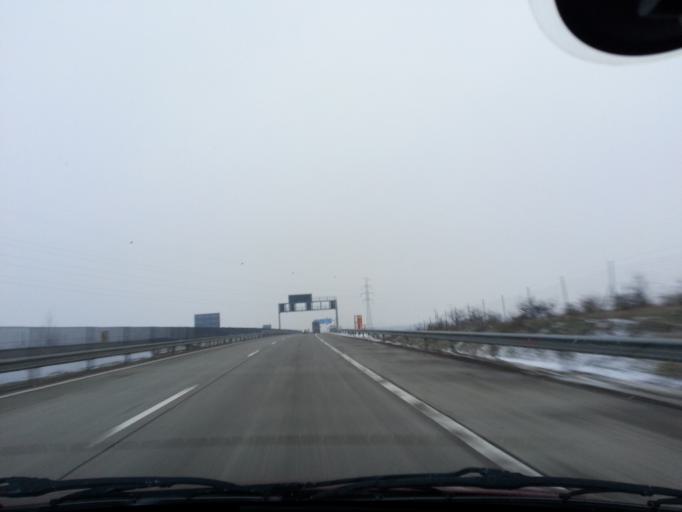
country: HU
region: Pest
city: Nagytarcsa
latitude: 47.5200
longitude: 19.3024
